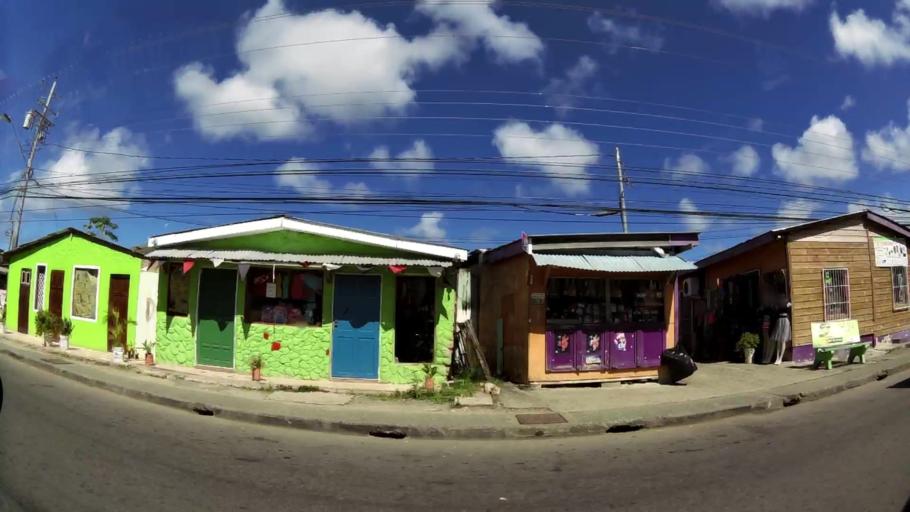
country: TT
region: Tobago
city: Scarborough
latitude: 11.1825
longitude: -60.7392
